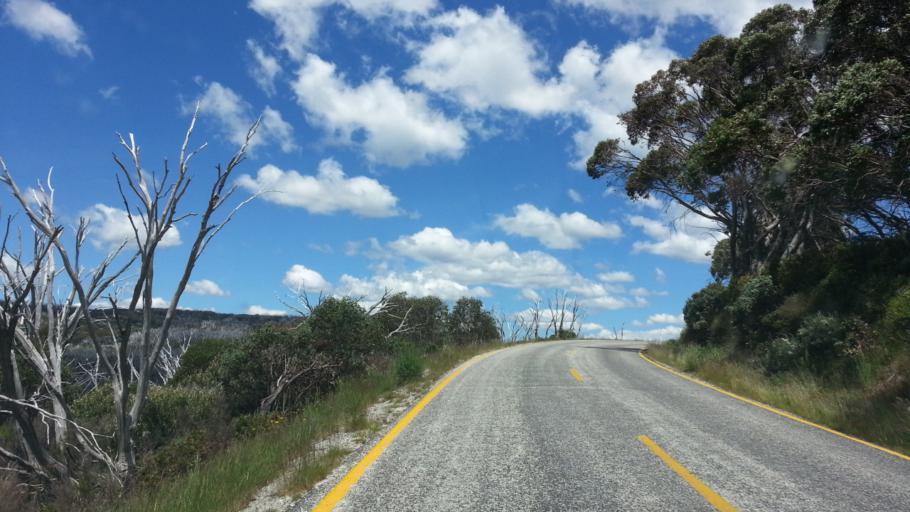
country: AU
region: Victoria
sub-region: Alpine
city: Mount Beauty
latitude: -36.8663
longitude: 147.2877
